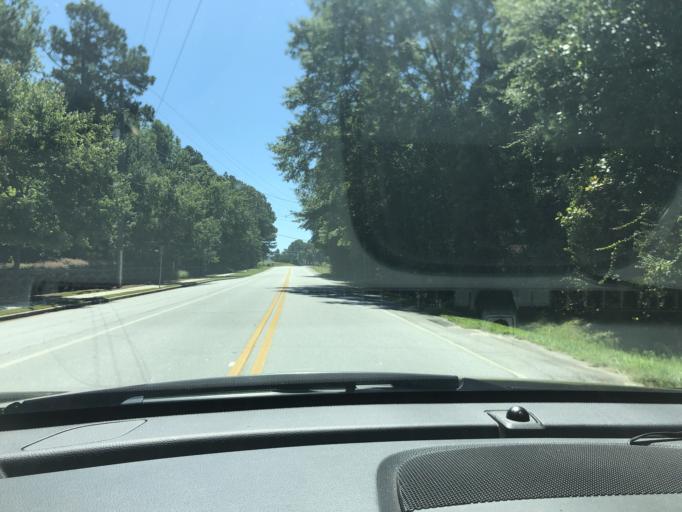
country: US
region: Georgia
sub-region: Gwinnett County
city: Grayson
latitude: 33.9089
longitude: -83.8911
